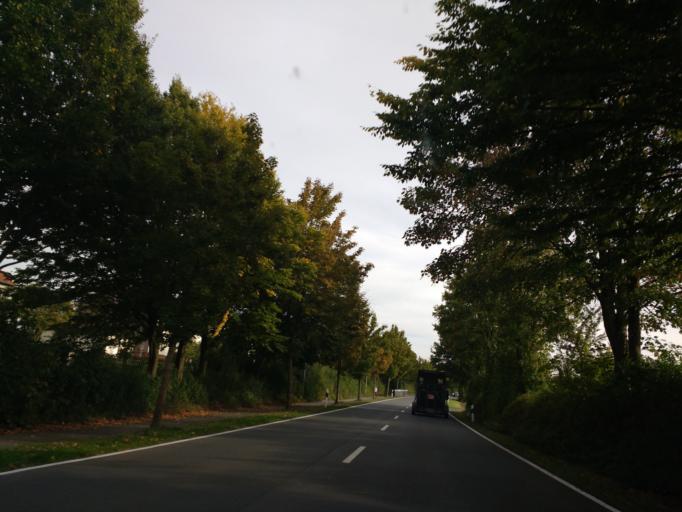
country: DE
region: North Rhine-Westphalia
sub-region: Regierungsbezirk Detmold
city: Bad Meinberg
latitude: 51.9389
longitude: 9.0237
